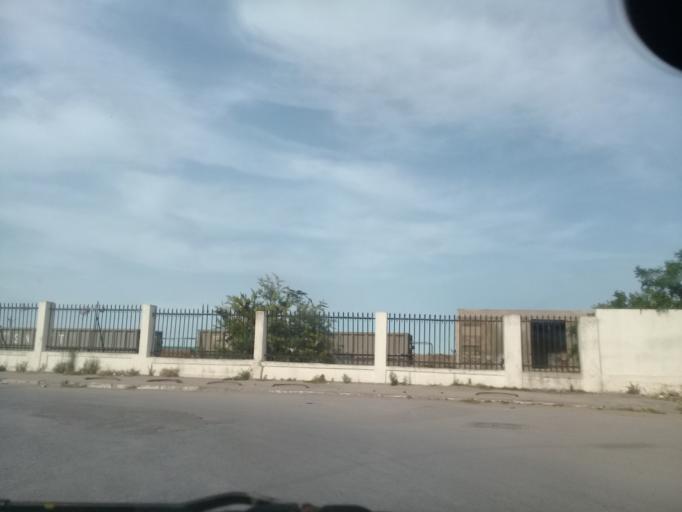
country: TN
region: Tunis
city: Tunis
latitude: 36.7906
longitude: 10.1879
